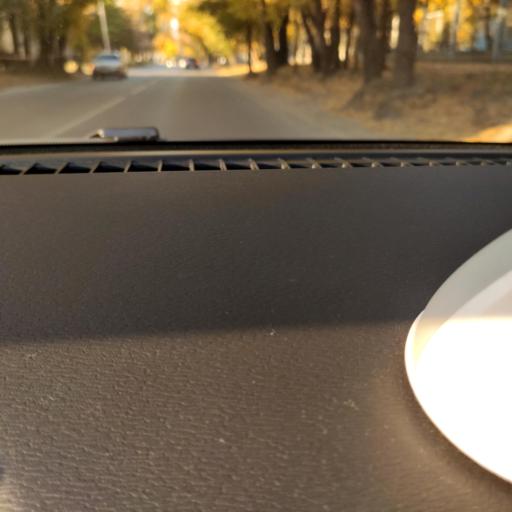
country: RU
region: Samara
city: Samara
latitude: 53.2271
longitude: 50.2368
